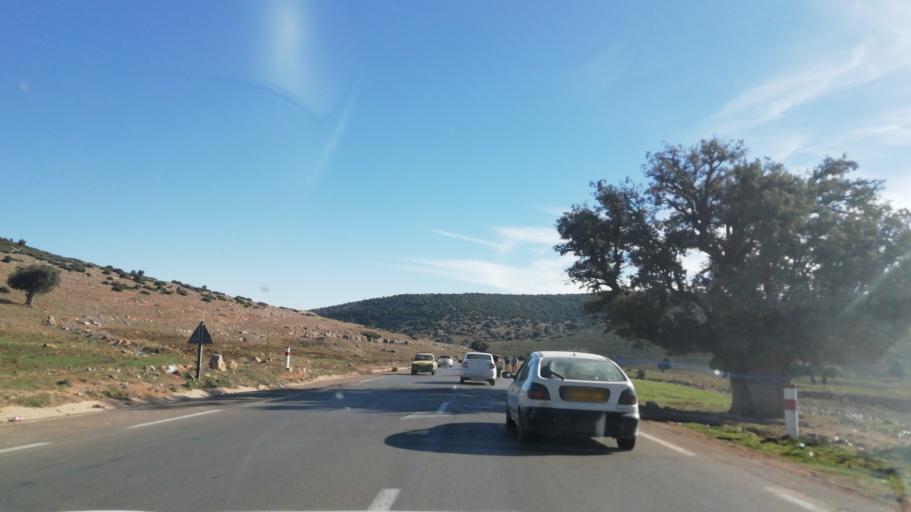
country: DZ
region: Tlemcen
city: Sebdou
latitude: 34.7195
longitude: -1.3382
